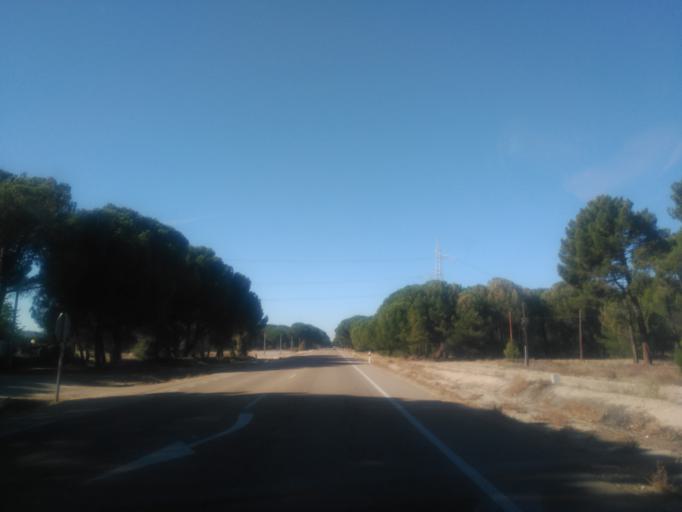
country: ES
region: Castille and Leon
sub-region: Provincia de Valladolid
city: Traspinedo
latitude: 41.5995
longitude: -4.4915
